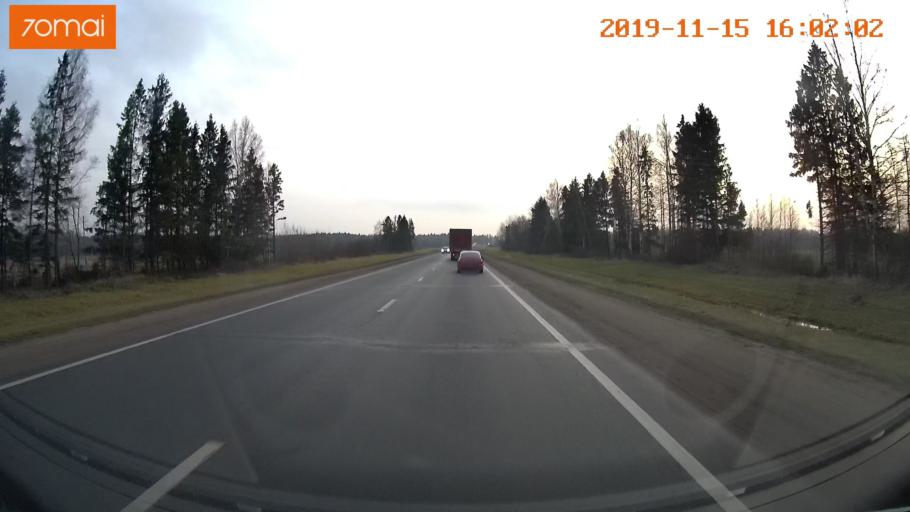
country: RU
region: Jaroslavl
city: Yaroslavl
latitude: 57.7761
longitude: 39.9274
